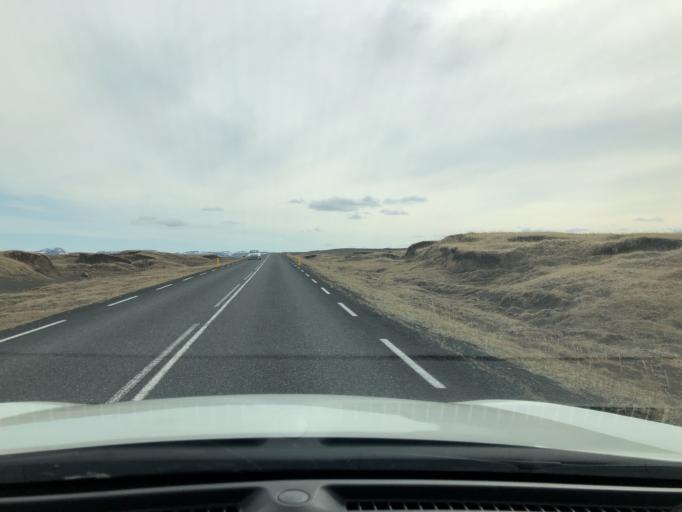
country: IS
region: Northeast
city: Laugar
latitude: 65.6391
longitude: -16.3078
